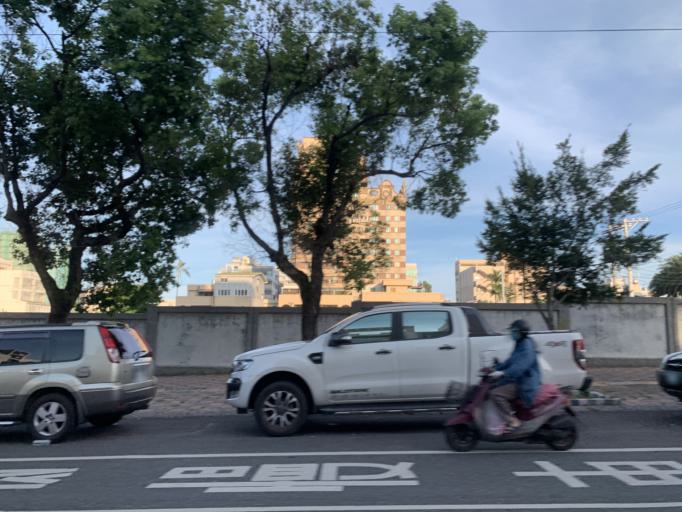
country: TW
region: Taiwan
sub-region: Hualien
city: Hualian
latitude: 23.9932
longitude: 121.6274
